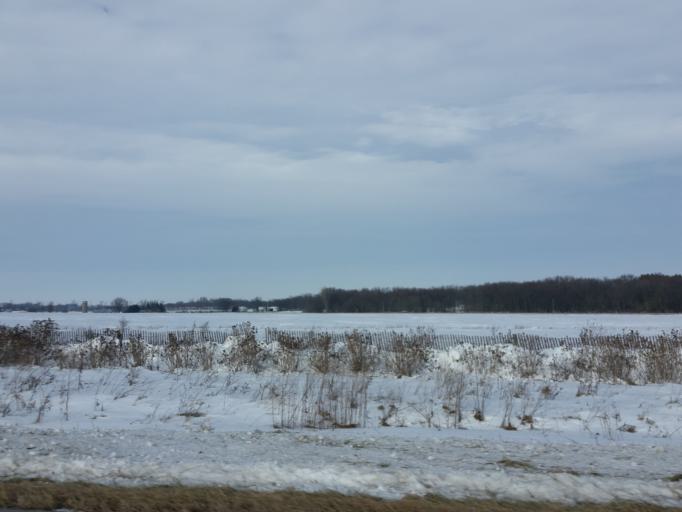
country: US
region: Iowa
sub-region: Buchanan County
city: Independence
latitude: 42.4610
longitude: -91.7169
